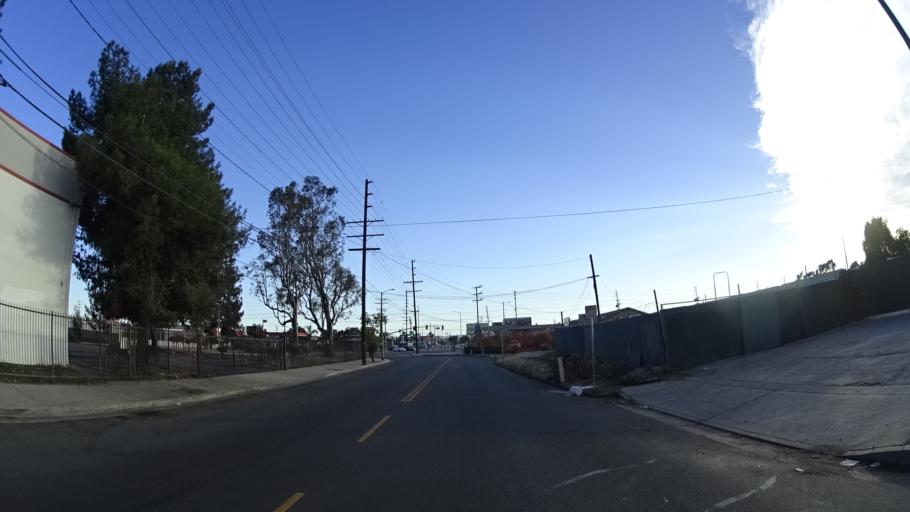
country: US
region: California
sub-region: Los Angeles County
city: North Hollywood
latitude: 34.2354
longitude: -118.3701
